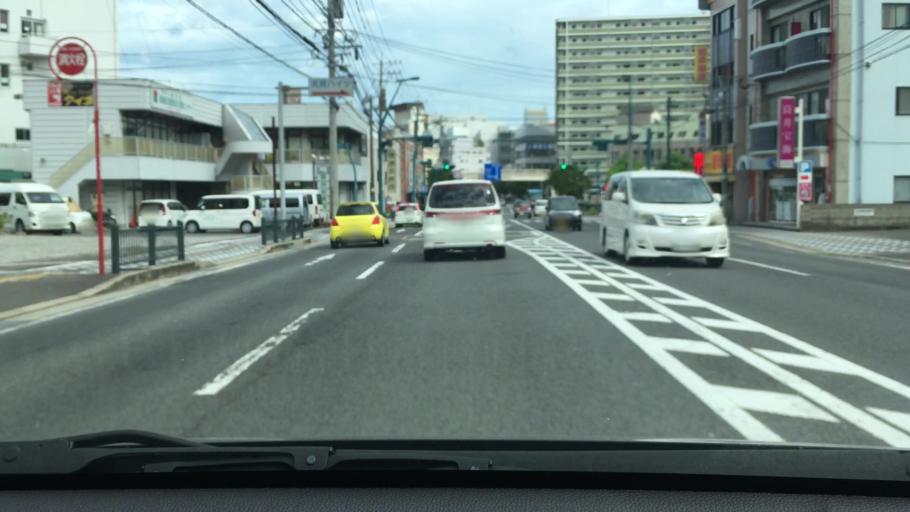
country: JP
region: Nagasaki
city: Togitsu
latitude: 32.8077
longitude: 129.8469
